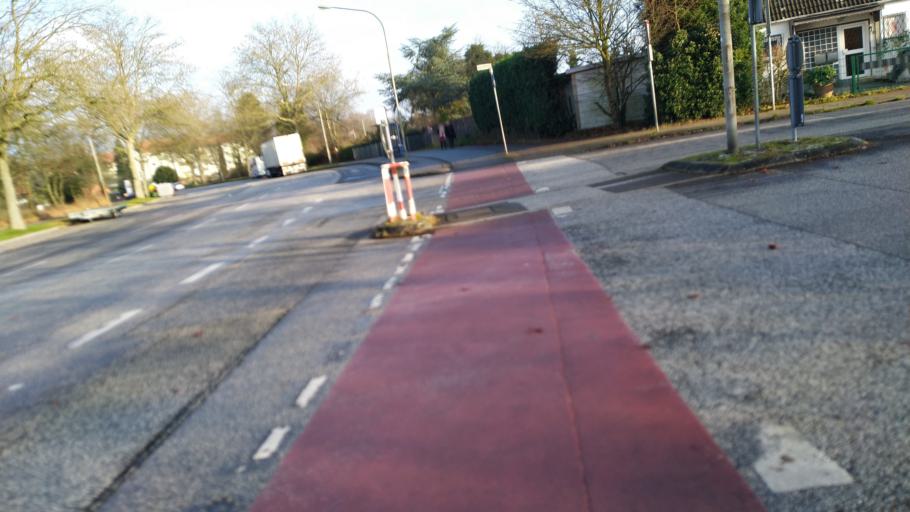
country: DE
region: Mecklenburg-Vorpommern
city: Selmsdorf
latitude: 53.9150
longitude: 10.8112
